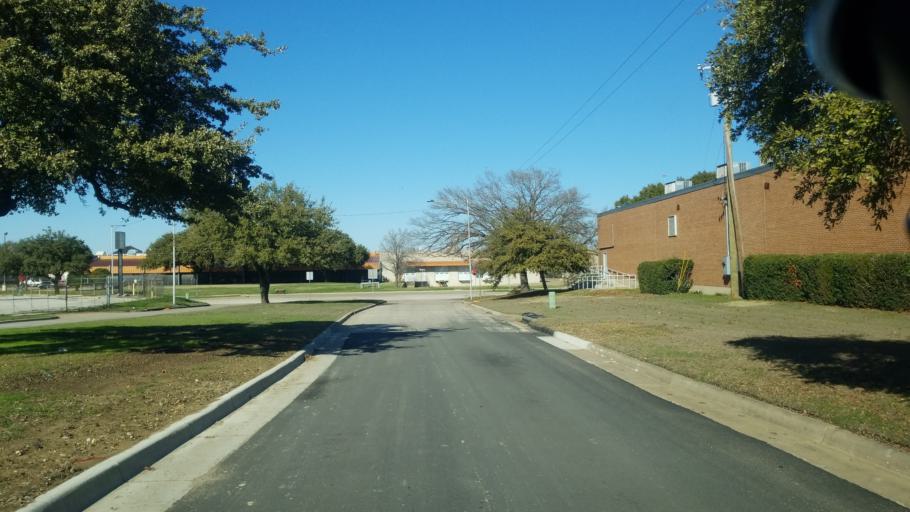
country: US
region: Texas
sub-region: Dallas County
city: Grand Prairie
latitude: 32.7557
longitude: -97.0542
